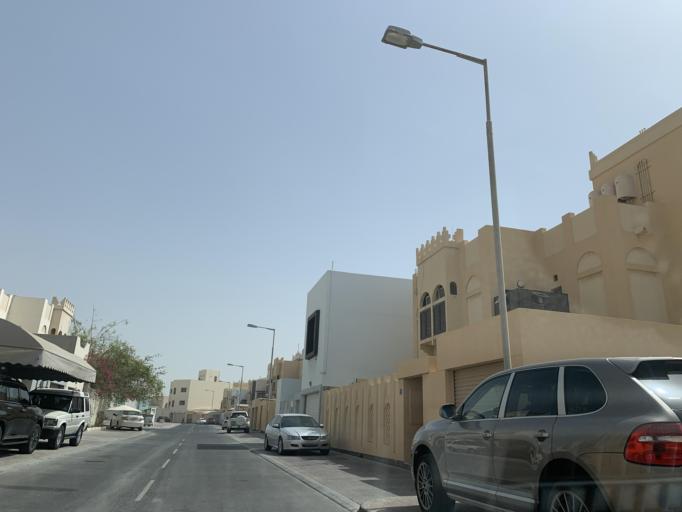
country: BH
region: Northern
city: Madinat `Isa
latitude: 26.1694
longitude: 50.5212
